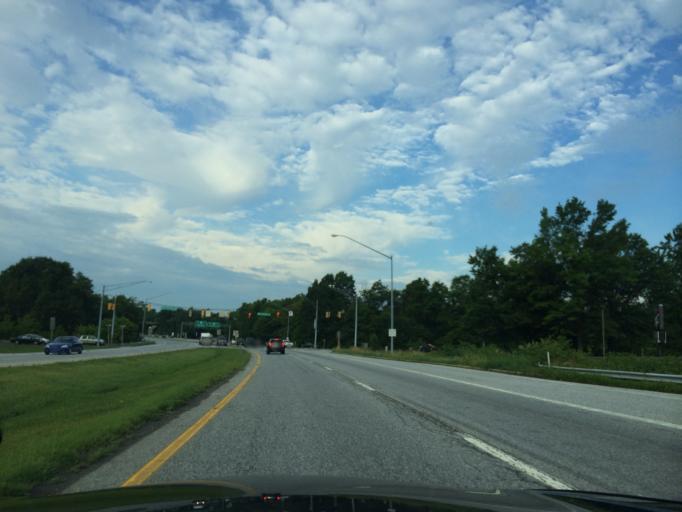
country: US
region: Maryland
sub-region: Carroll County
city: Mount Airy
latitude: 39.3626
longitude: -77.1628
